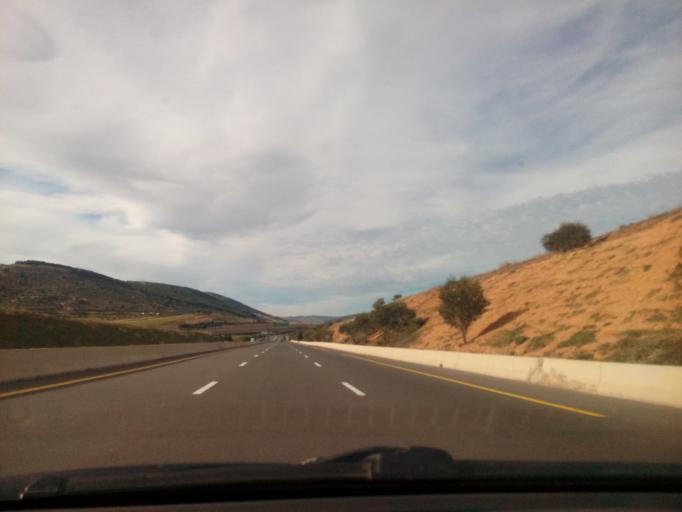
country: DZ
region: Sidi Bel Abbes
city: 'Ain el Berd
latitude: 35.4409
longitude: -0.4194
